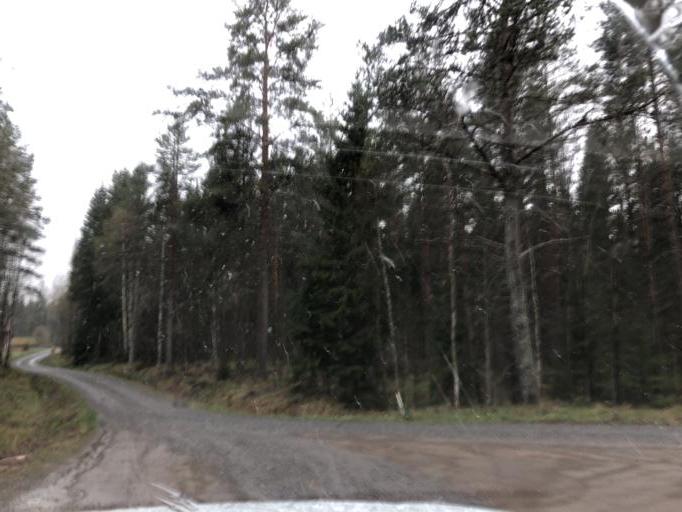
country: SE
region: Uppsala
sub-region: Heby Kommun
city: Tarnsjo
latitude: 60.2077
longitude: 16.8920
